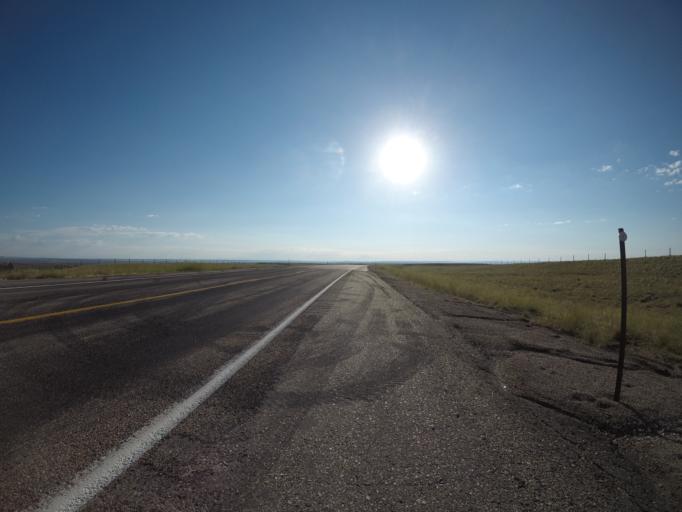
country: US
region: Wyoming
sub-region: Lincoln County
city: Kemmerer
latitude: 41.8923
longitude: -110.3499
